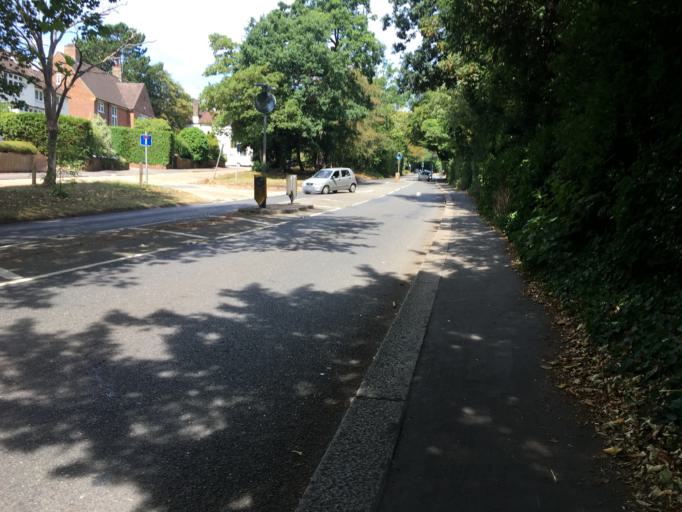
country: GB
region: England
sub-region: Surrey
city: Reigate
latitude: 51.2258
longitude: -0.2002
